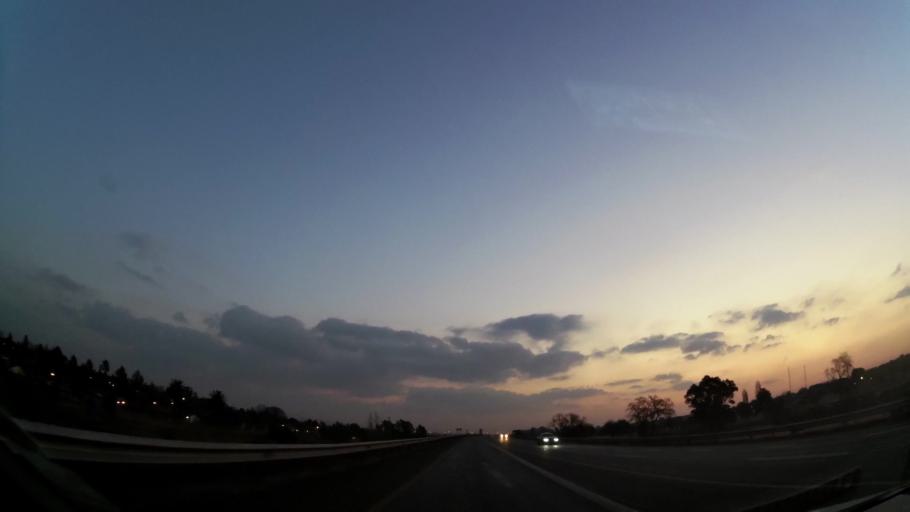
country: ZA
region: Gauteng
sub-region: Ekurhuleni Metropolitan Municipality
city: Springs
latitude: -26.2815
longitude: 28.4475
